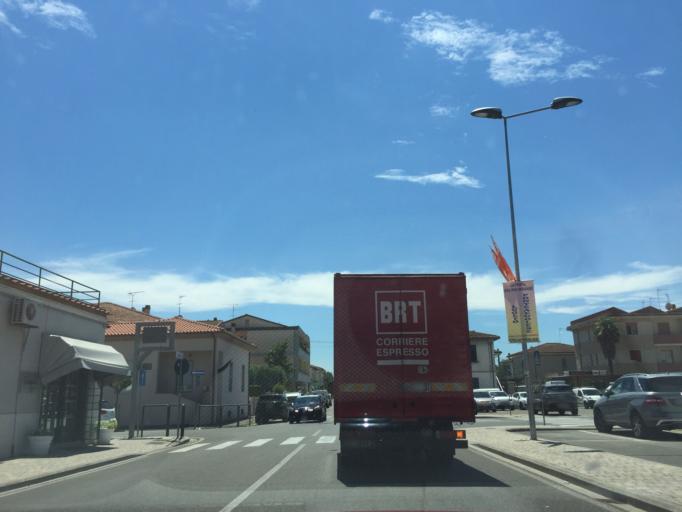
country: IT
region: Tuscany
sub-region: Province of Pisa
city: San Miniato
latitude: 43.6857
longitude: 10.7935
